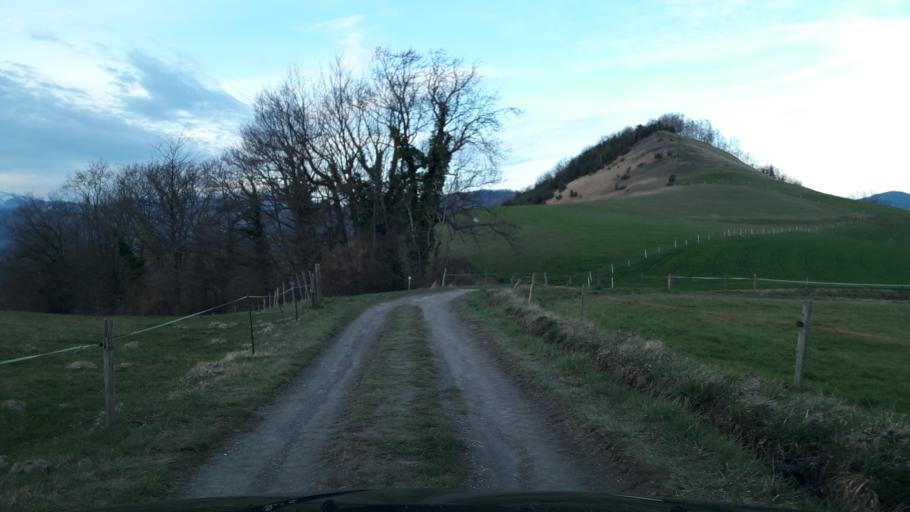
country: FR
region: Rhone-Alpes
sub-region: Departement de l'Isere
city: Brie-et-Angonnes
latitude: 45.1085
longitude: 5.7763
